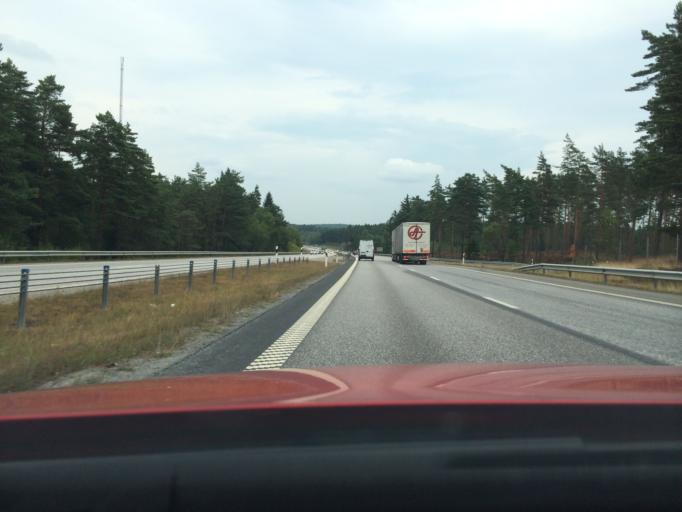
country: SE
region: OEstergoetland
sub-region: Norrkopings Kommun
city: Krokek
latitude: 58.6819
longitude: 16.3211
